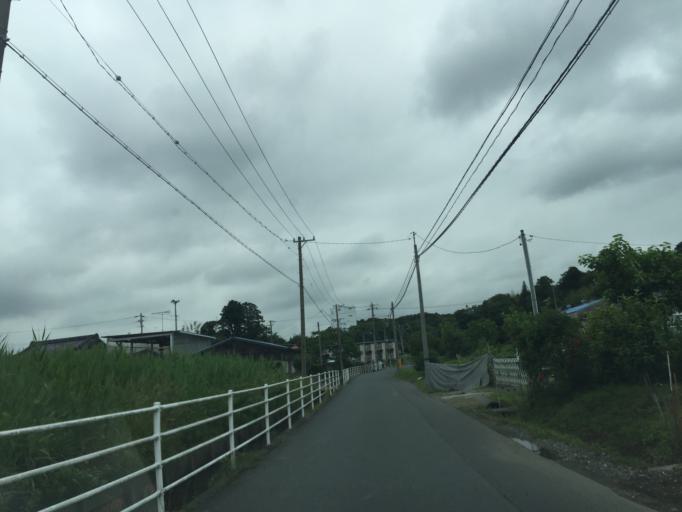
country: JP
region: Shizuoka
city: Fukuroi
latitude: 34.7655
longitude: 137.9276
